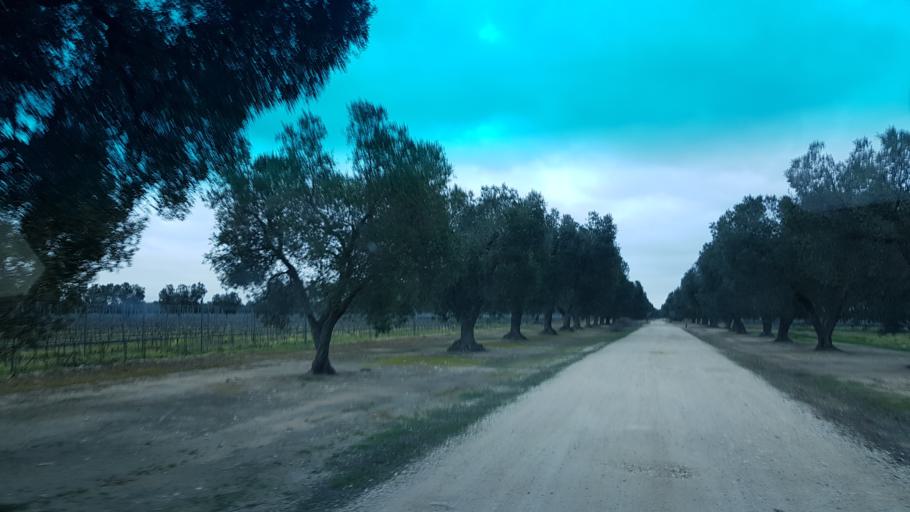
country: IT
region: Apulia
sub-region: Provincia di Brindisi
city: La Rosa
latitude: 40.5921
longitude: 17.9799
